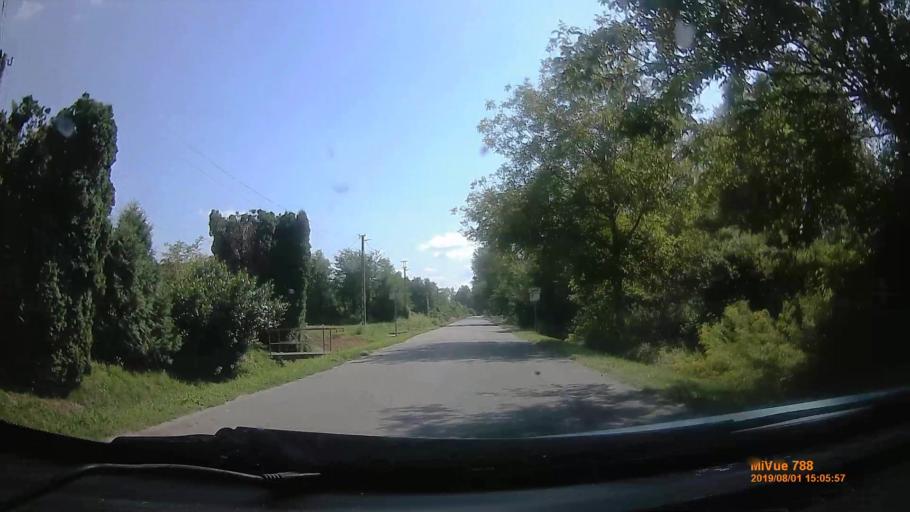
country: HU
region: Baranya
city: Sellye
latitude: 45.8685
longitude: 17.8414
